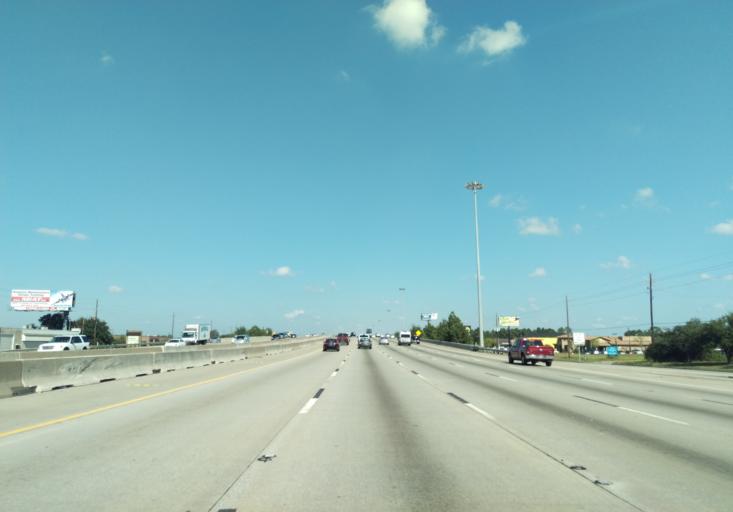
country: US
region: Texas
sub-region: Harris County
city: Aldine
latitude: 29.9937
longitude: -95.4247
